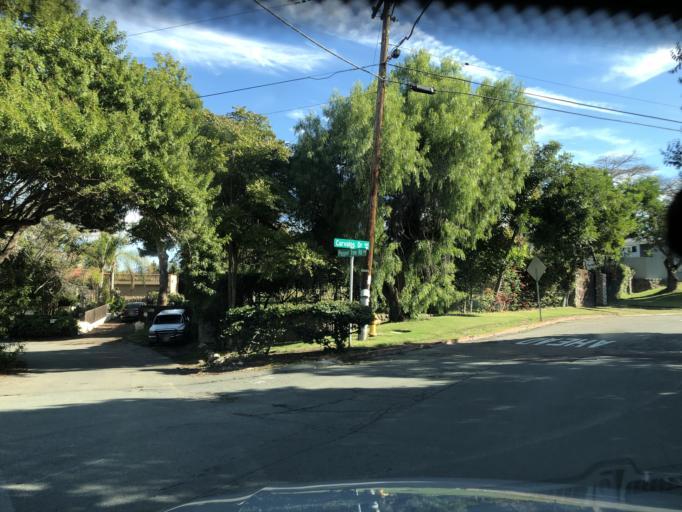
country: US
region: California
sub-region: San Diego County
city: Chula Vista
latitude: 32.6428
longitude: -117.0610
